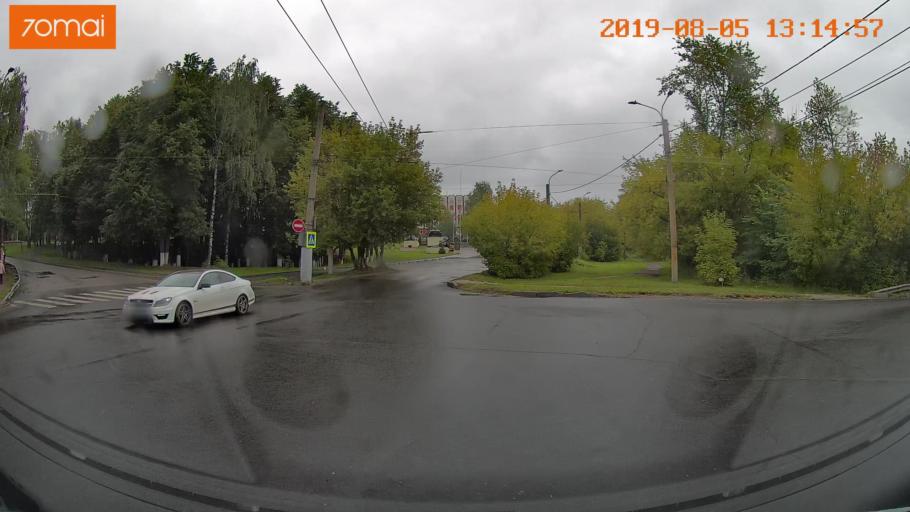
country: RU
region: Ivanovo
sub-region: Gorod Ivanovo
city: Ivanovo
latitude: 56.9936
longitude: 41.0181
